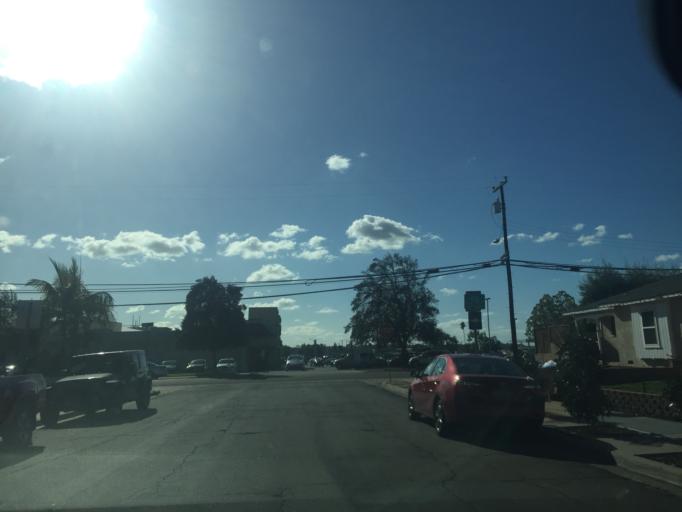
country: US
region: California
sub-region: San Diego County
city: La Mesa
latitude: 32.7926
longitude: -117.0797
